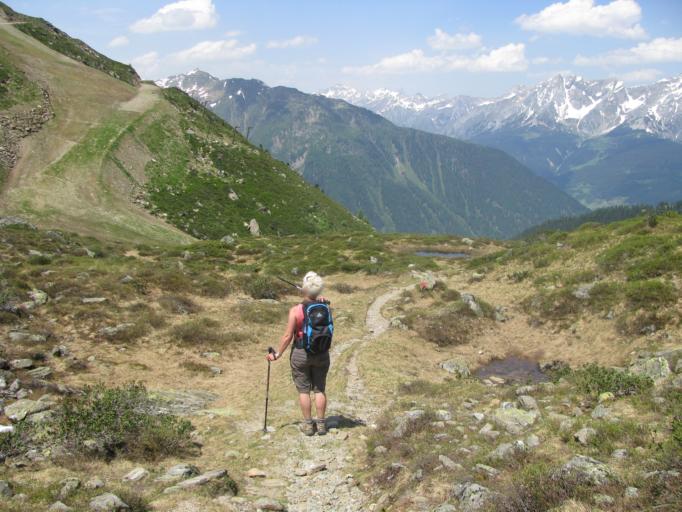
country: AT
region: Tyrol
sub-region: Politischer Bezirk Landeck
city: See
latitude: 47.0657
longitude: 10.5004
